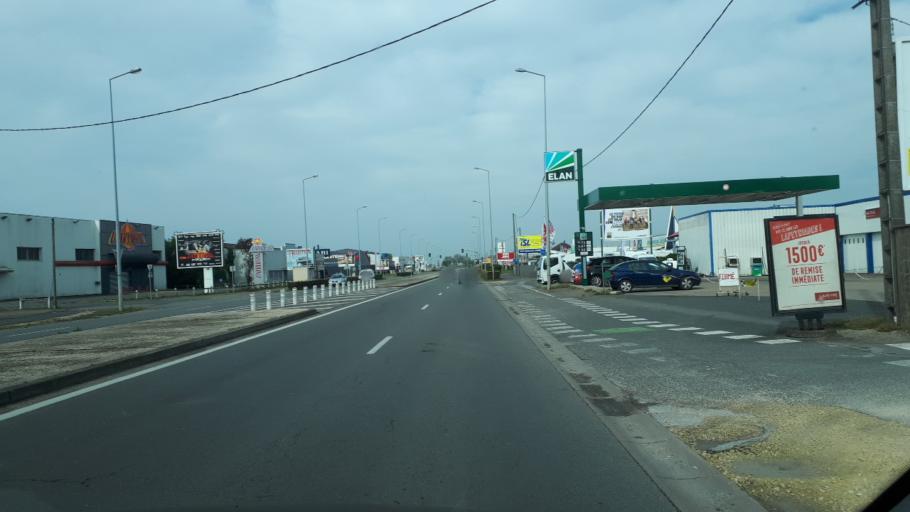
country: FR
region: Centre
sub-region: Departement du Cher
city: Saint-Germain-du-Puy
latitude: 47.0969
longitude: 2.4511
